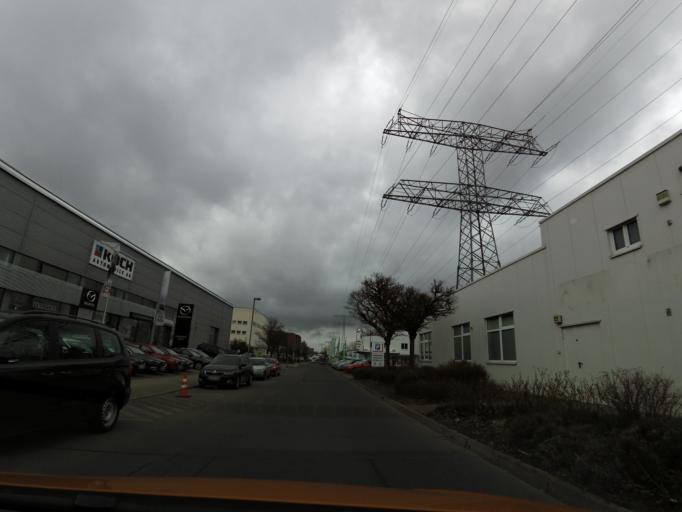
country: DE
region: Berlin
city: Biesdorf
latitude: 52.5277
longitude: 13.5345
